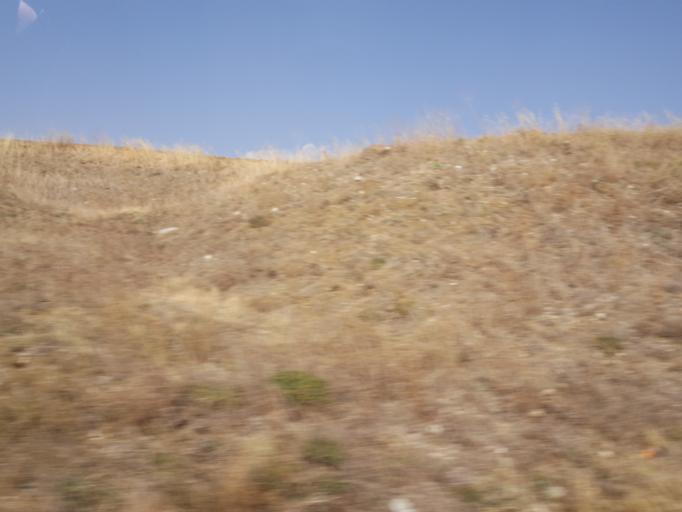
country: TR
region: Corum
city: Bogazkale
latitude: 40.1586
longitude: 34.6242
